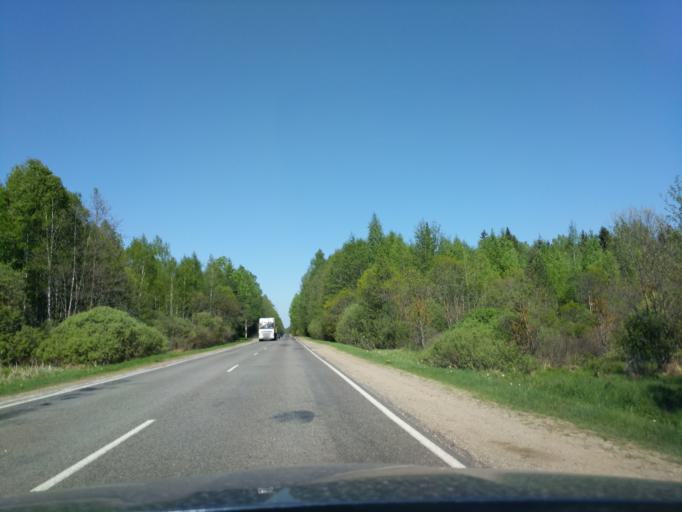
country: BY
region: Minsk
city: Il'ya
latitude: 54.4010
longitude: 27.3272
